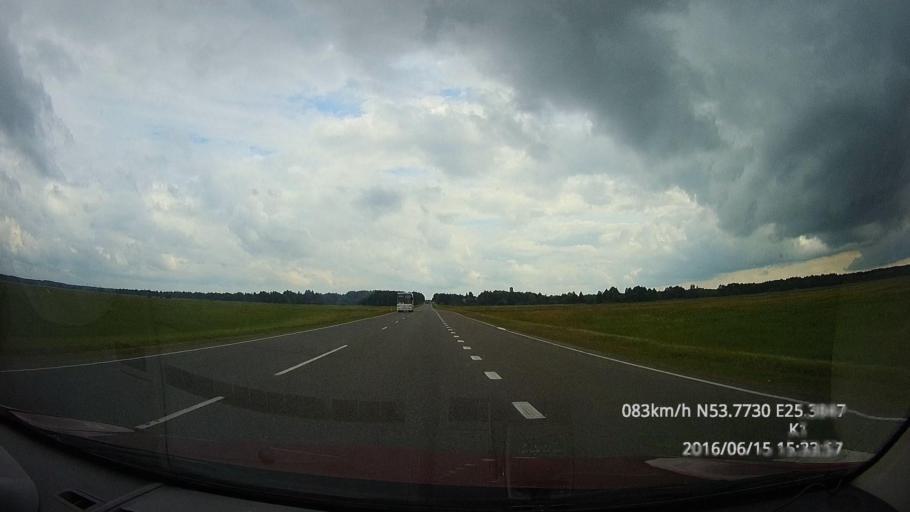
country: BY
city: Berezovka
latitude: 53.7725
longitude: 25.3850
